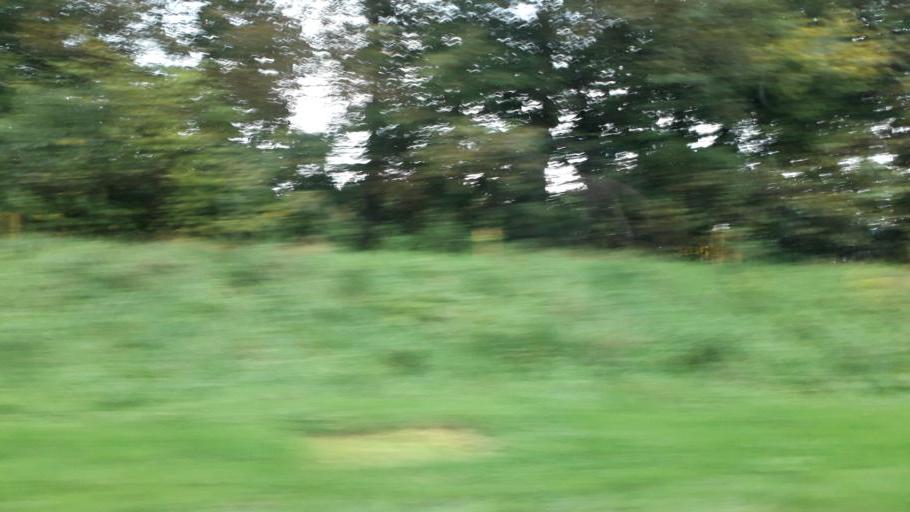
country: IE
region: Leinster
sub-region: An Longfort
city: Longford
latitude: 53.7436
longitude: -7.8066
